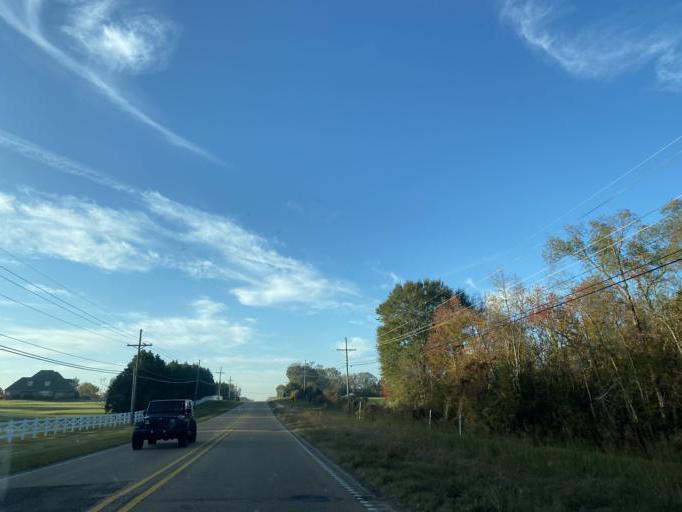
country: US
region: Mississippi
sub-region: Madison County
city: Madison
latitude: 32.5058
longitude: -90.0886
